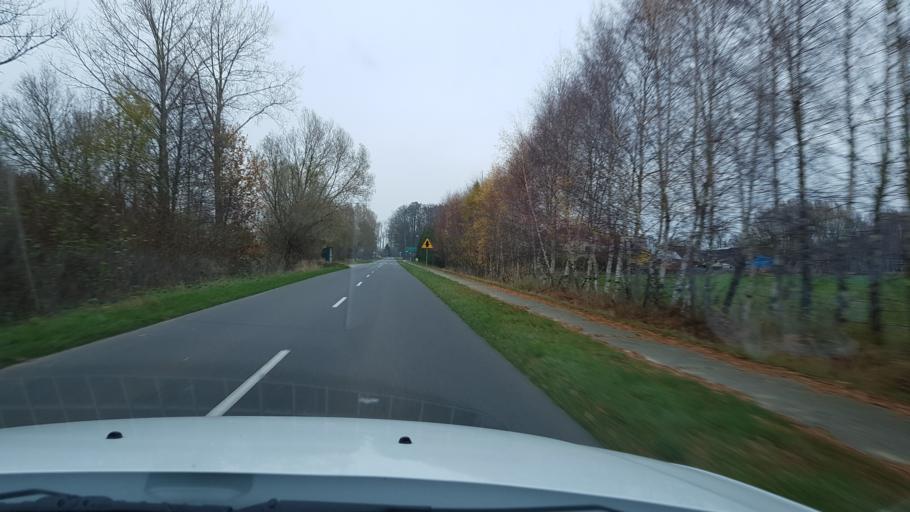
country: PL
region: West Pomeranian Voivodeship
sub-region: Powiat kamienski
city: Kamien Pomorski
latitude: 53.9482
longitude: 14.6796
